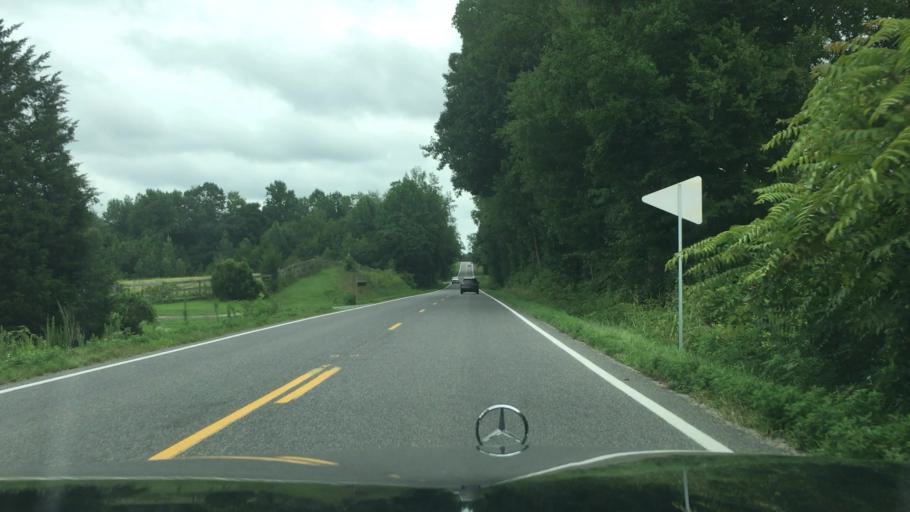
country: US
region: Virginia
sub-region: Nottoway County
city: Crewe
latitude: 37.2789
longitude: -78.2116
